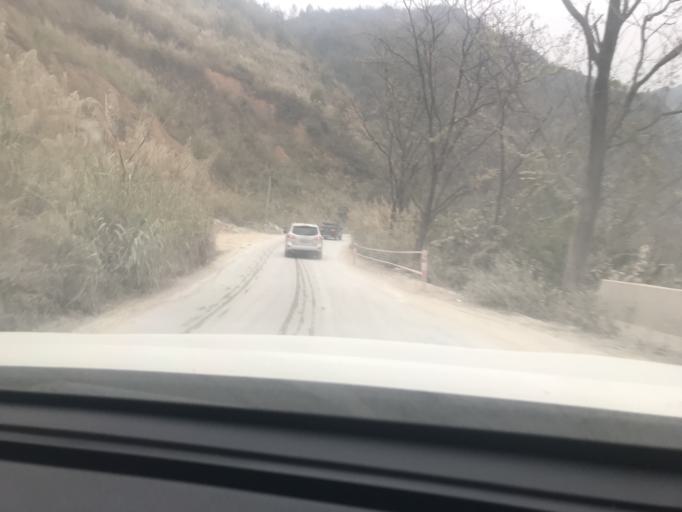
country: CN
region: Guangxi Zhuangzu Zizhiqu
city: Xinzhou
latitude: 24.9942
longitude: 105.8223
